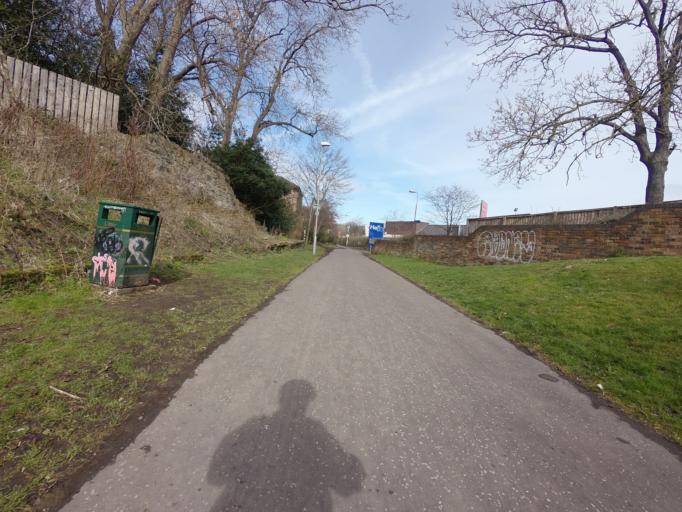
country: GB
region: Scotland
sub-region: Edinburgh
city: Edinburgh
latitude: 55.9629
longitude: -3.1967
